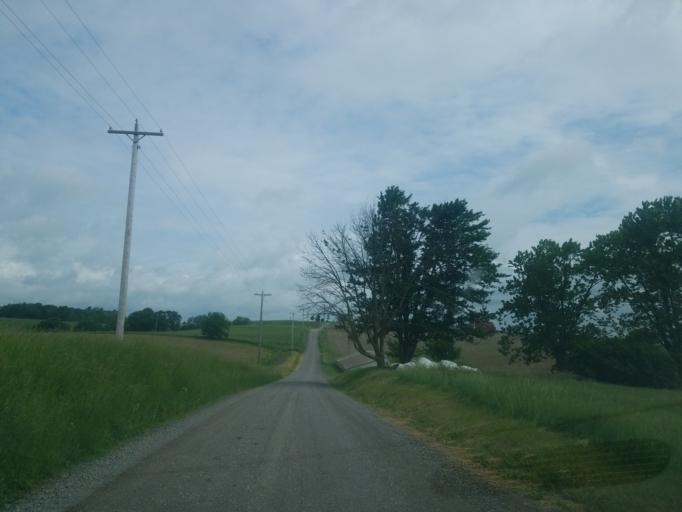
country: US
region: Ohio
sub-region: Tuscarawas County
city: Sugarcreek
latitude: 40.5023
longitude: -81.7697
